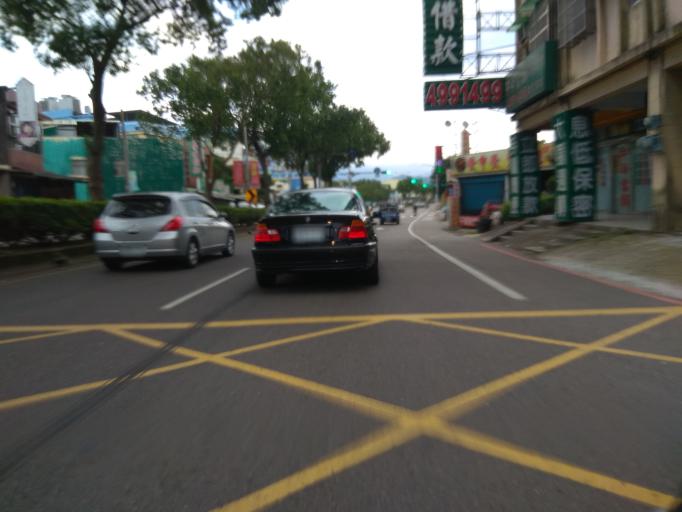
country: TW
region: Taiwan
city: Daxi
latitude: 24.8758
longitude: 121.2131
